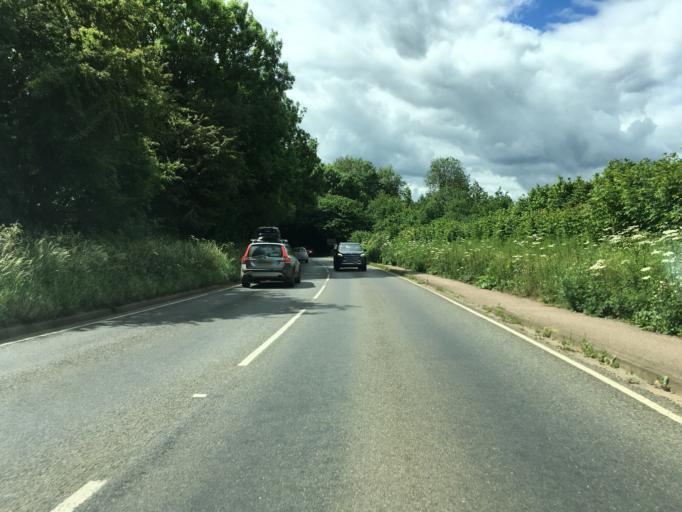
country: GB
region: England
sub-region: Oxfordshire
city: Bloxham
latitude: 52.0377
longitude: -1.3637
